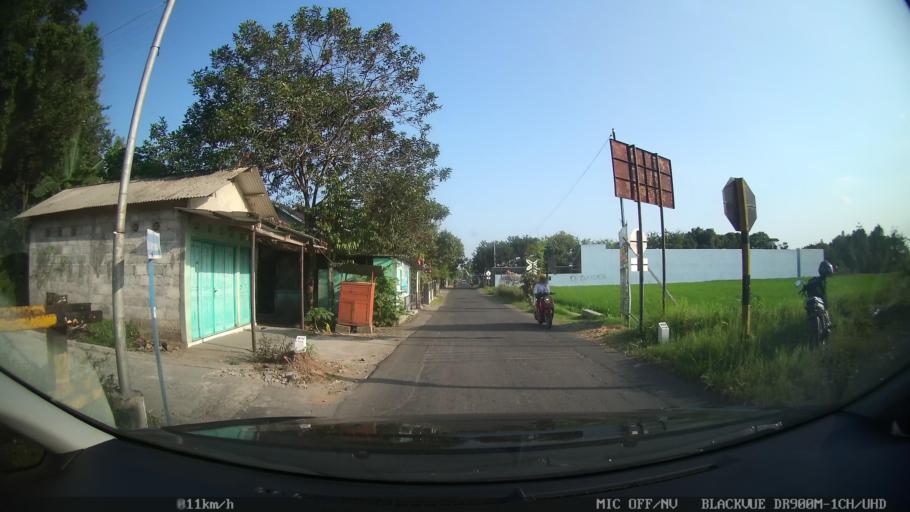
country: ID
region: Daerah Istimewa Yogyakarta
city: Gamping Lor
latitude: -7.7893
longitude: 110.3336
